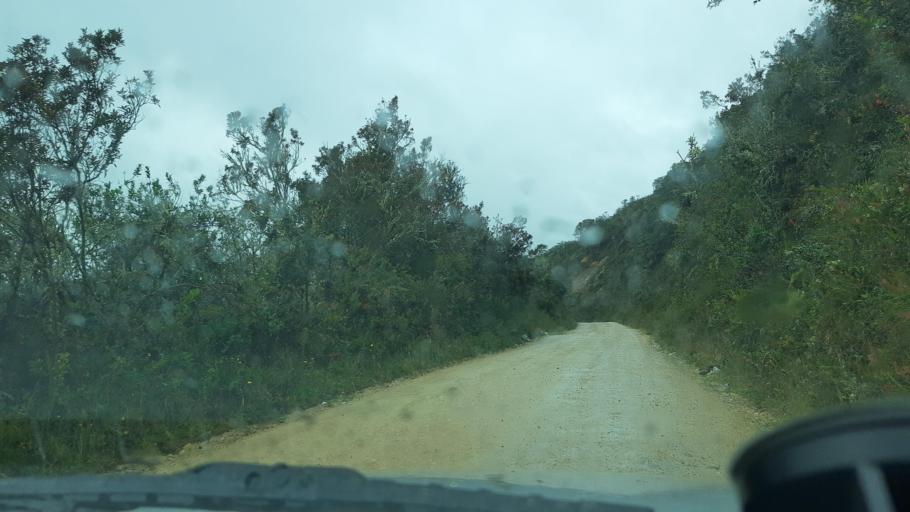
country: CO
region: Cundinamarca
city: Villapinzon
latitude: 5.2112
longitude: -73.5736
